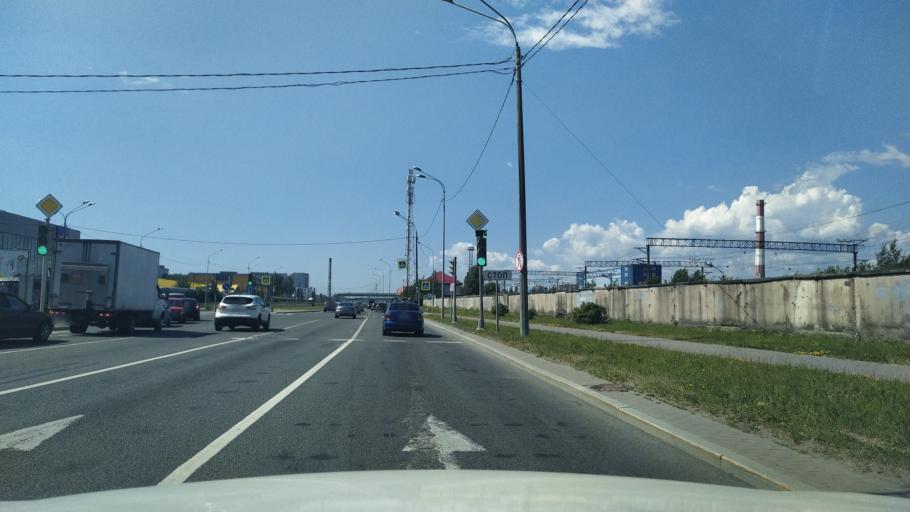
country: RU
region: Leningrad
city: Parnas
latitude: 60.0566
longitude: 30.3614
